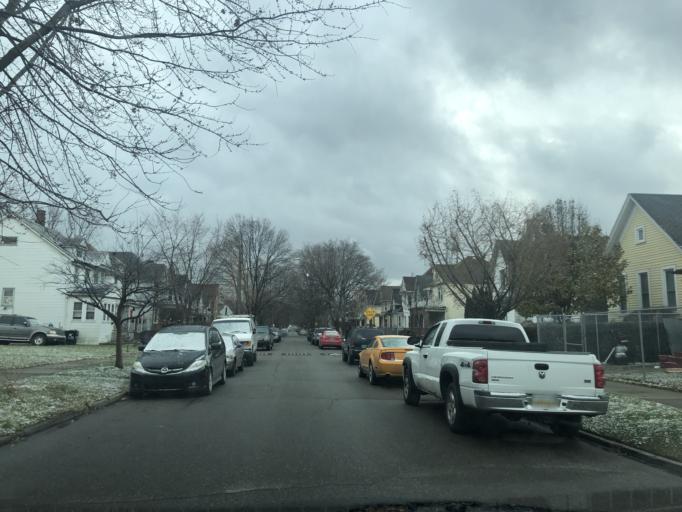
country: US
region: Michigan
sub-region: Wayne County
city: Detroit
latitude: 42.3184
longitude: -83.0992
